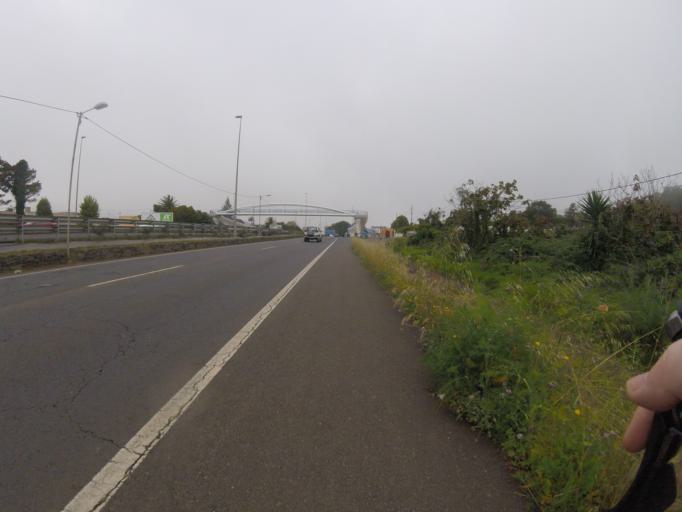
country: ES
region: Canary Islands
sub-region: Provincia de Santa Cruz de Tenerife
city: La Laguna
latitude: 28.4913
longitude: -16.3616
